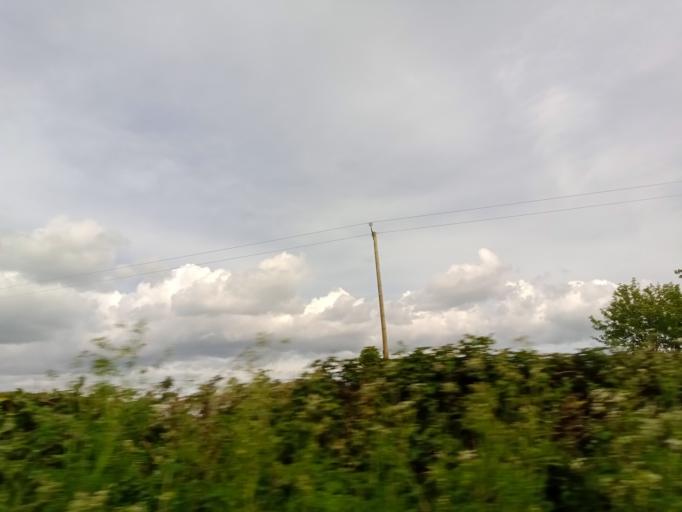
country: IE
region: Munster
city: Thurles
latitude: 52.6164
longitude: -7.7887
